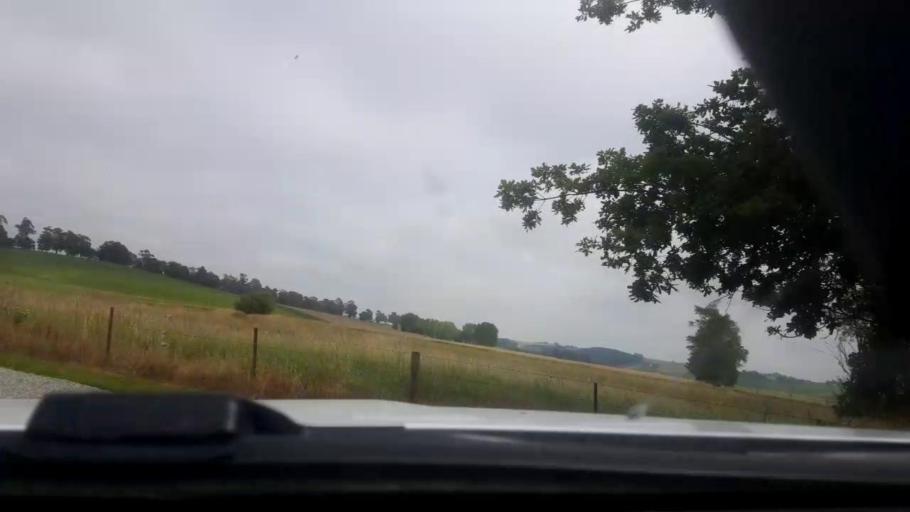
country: NZ
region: Canterbury
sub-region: Timaru District
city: Pleasant Point
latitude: -44.3220
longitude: 171.1924
